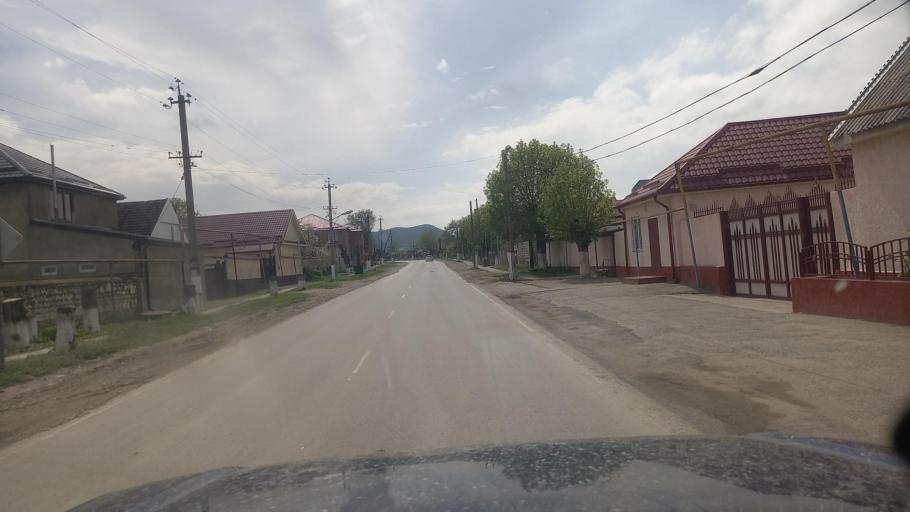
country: RU
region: Kabardino-Balkariya
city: Sarmakovo
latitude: 43.7390
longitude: 43.1849
